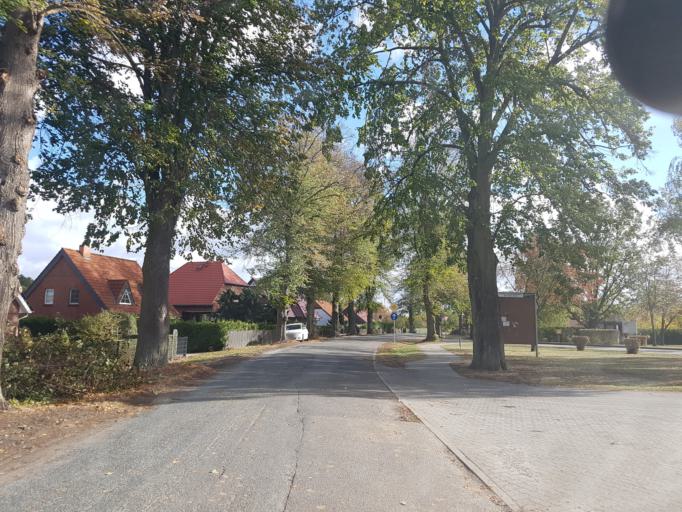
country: DE
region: Brandenburg
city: Nauen
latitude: 52.6634
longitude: 12.9077
